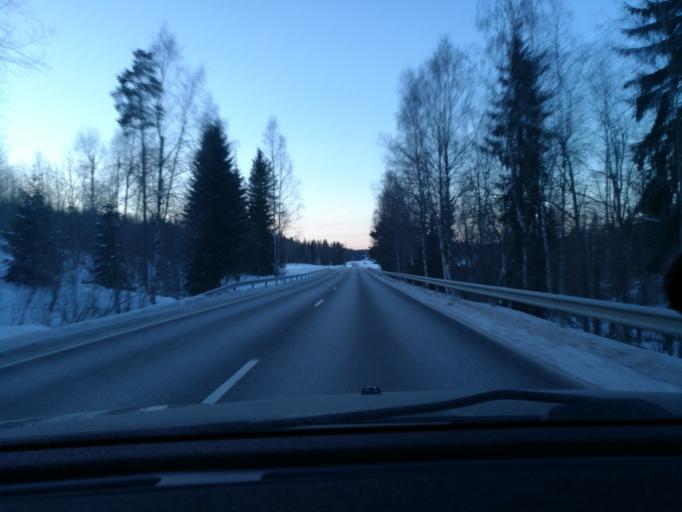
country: FI
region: Uusimaa
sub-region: Helsinki
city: Vihti
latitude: 60.4266
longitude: 24.4321
